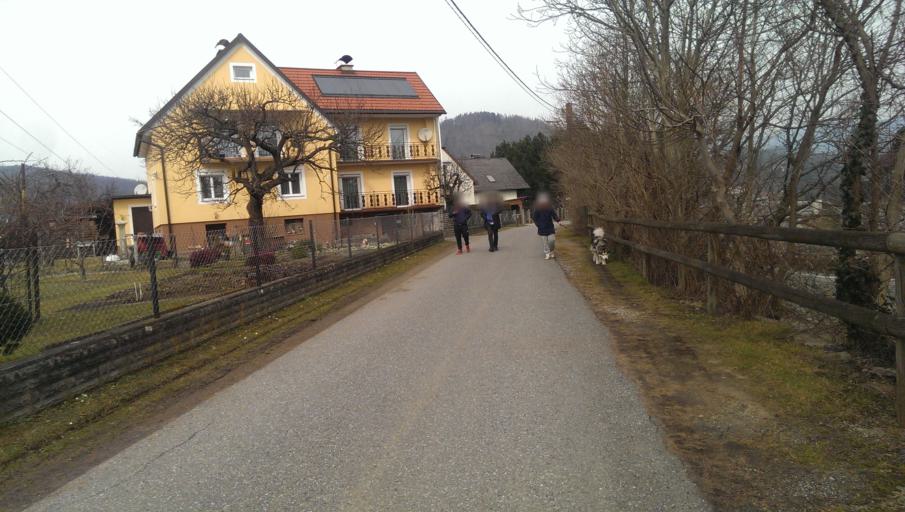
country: AT
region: Styria
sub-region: Graz Stadt
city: Goesting
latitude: 47.1028
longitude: 15.3980
